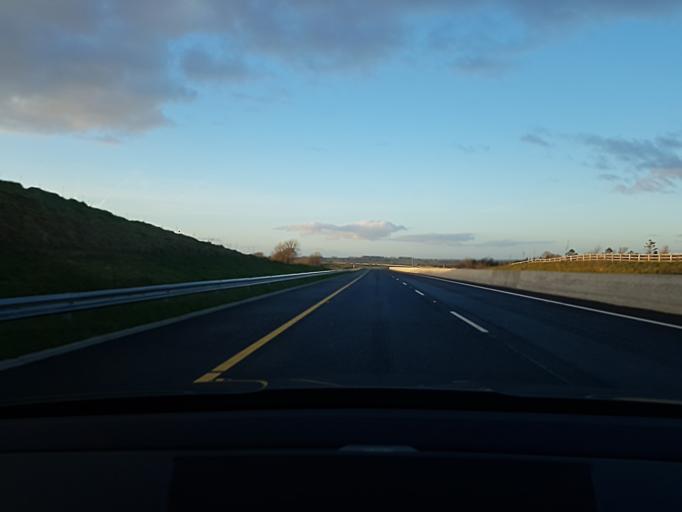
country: IE
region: Connaught
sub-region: County Galway
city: Tuam
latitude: 53.4119
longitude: -8.8274
